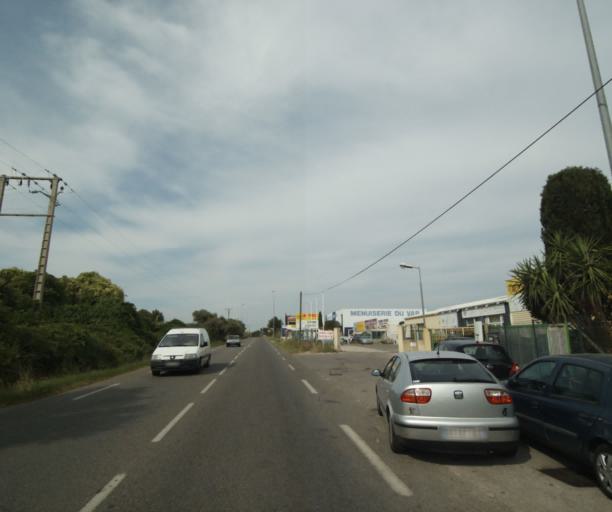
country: FR
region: Provence-Alpes-Cote d'Azur
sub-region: Departement du Var
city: La Farlede
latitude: 43.1535
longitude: 6.0371
